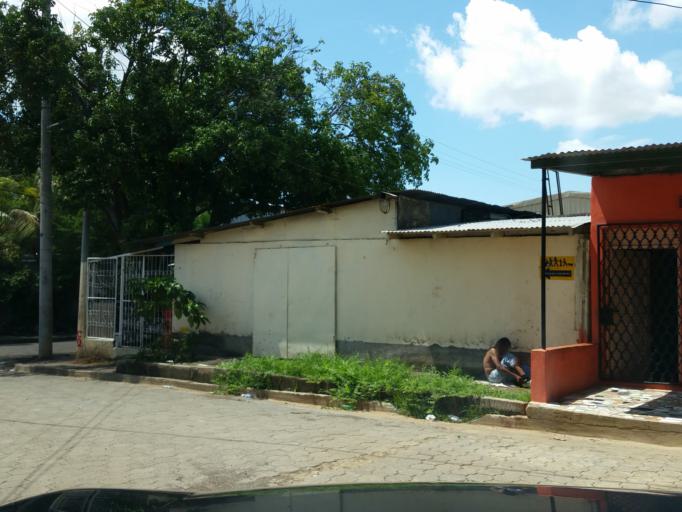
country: NI
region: Managua
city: Managua
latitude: 12.1181
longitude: -86.2459
